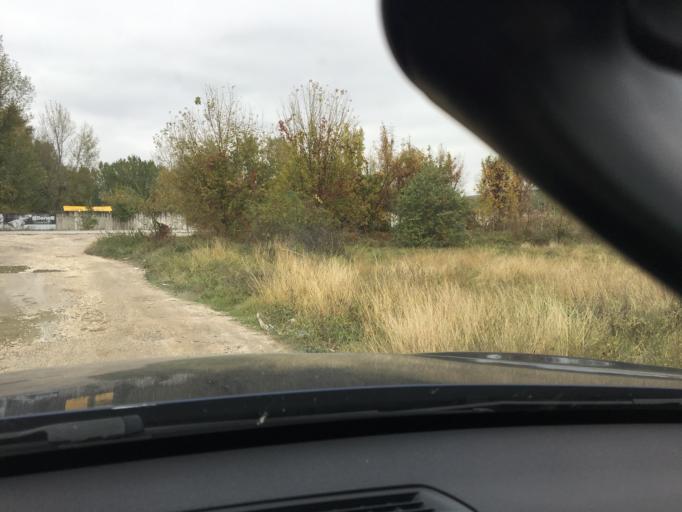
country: BG
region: Pleven
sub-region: Obshtina Dolna Mitropoliya
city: Dolna Mitropoliya
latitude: 43.4436
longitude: 24.5552
